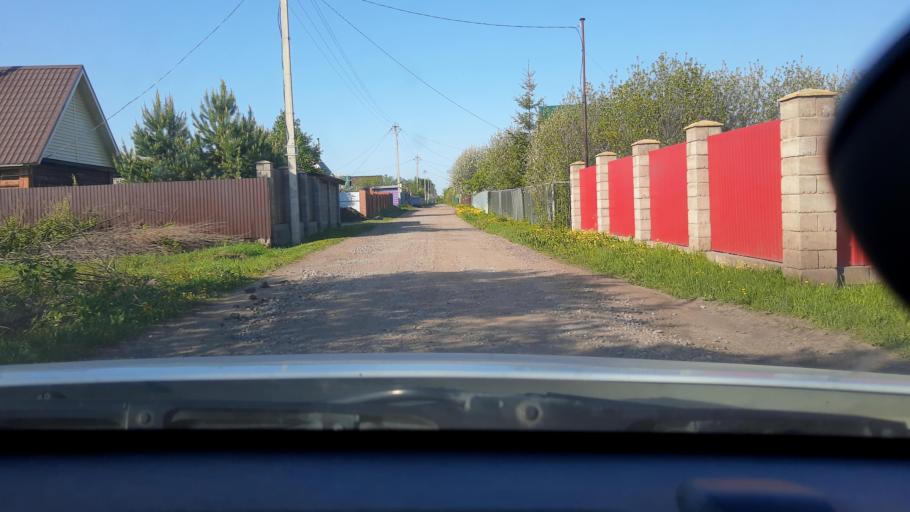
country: RU
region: Bashkortostan
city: Kabakovo
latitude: 54.4729
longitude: 55.9311
